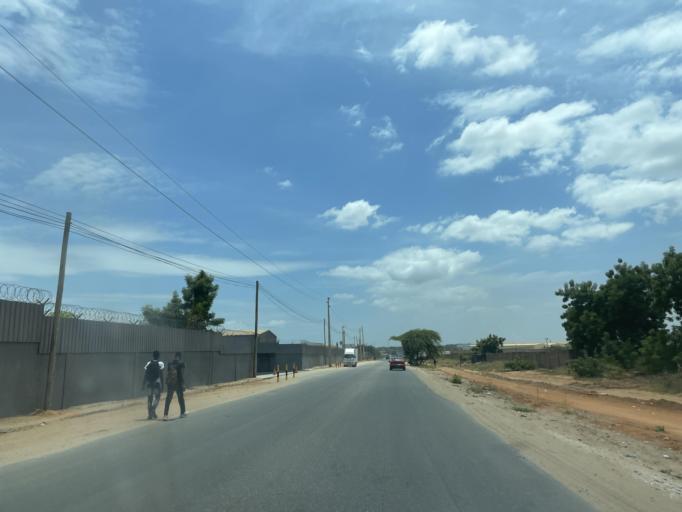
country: AO
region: Luanda
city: Luanda
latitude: -8.9397
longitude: 13.3882
